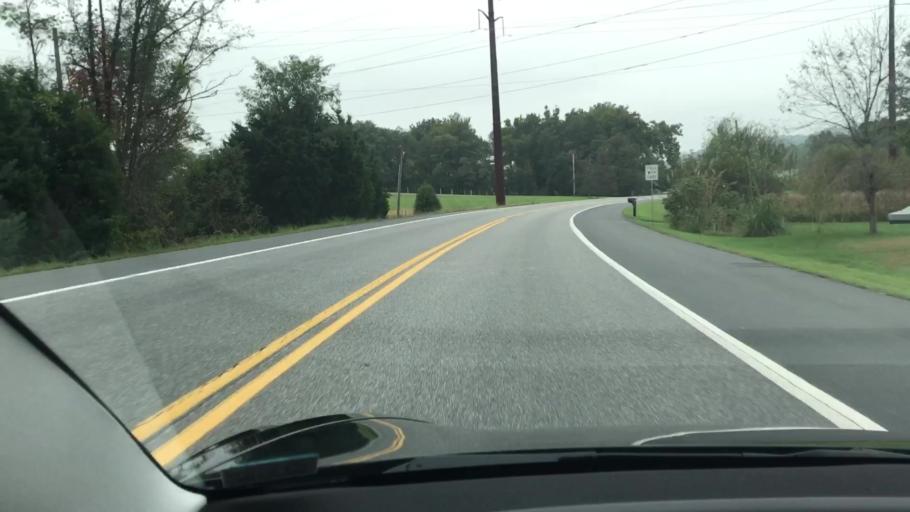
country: US
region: Pennsylvania
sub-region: Cumberland County
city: Lower Allen
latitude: 40.1550
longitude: -76.8836
